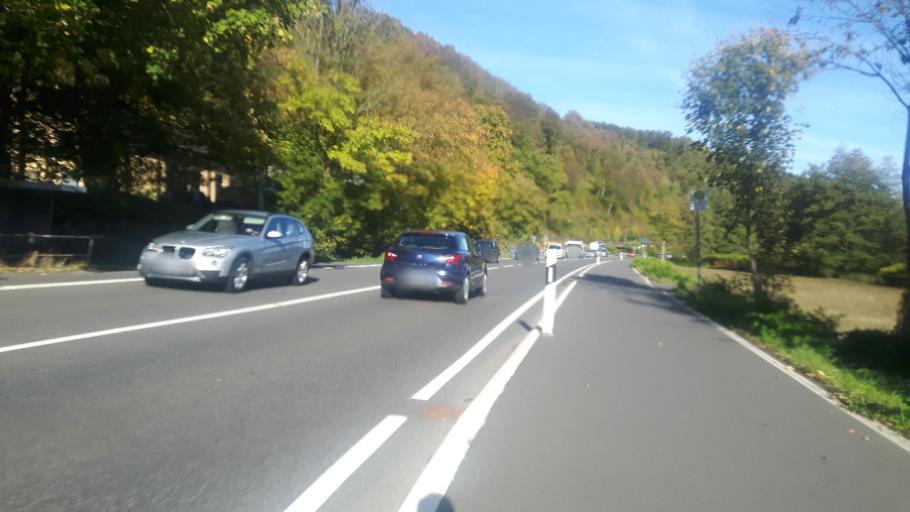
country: DE
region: Rheinland-Pfalz
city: Mittelhof
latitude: 50.8040
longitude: 7.7868
